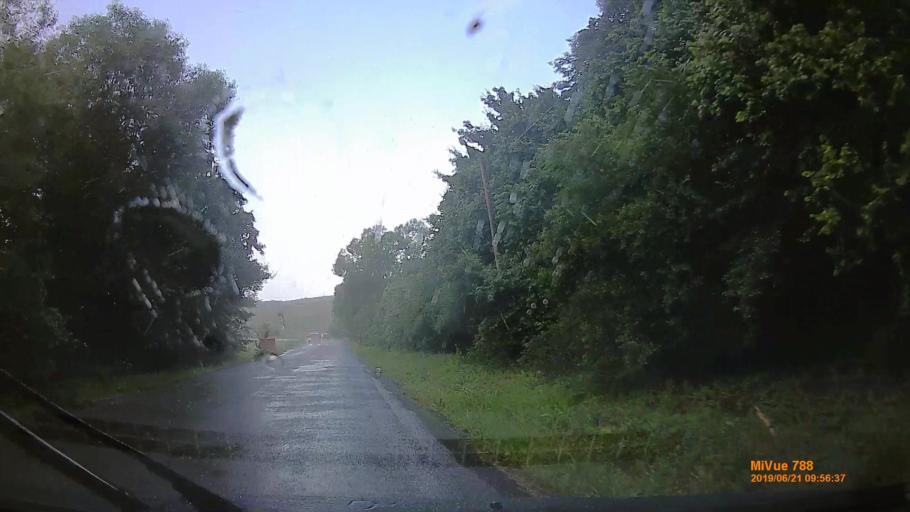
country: HU
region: Baranya
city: Buekkoesd
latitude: 46.2246
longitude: 17.9785
